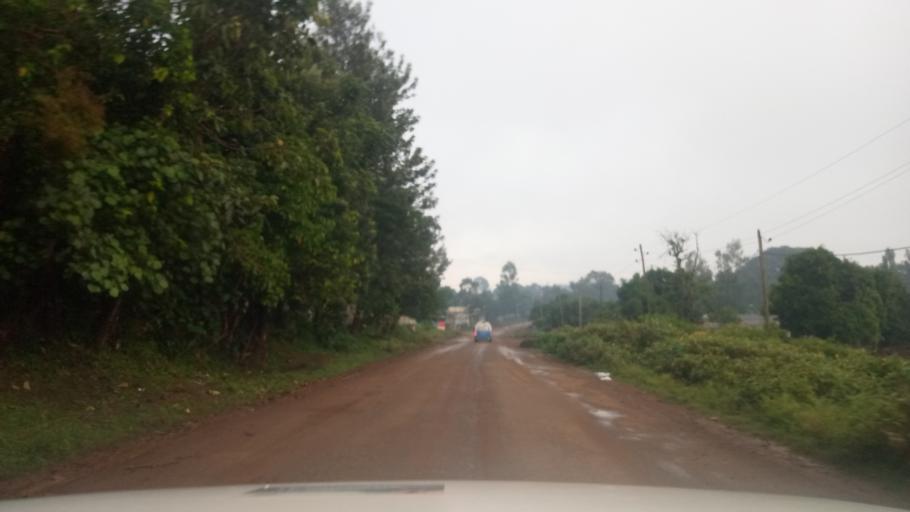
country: ET
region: Oromiya
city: Jima
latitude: 7.6937
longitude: 36.8203
